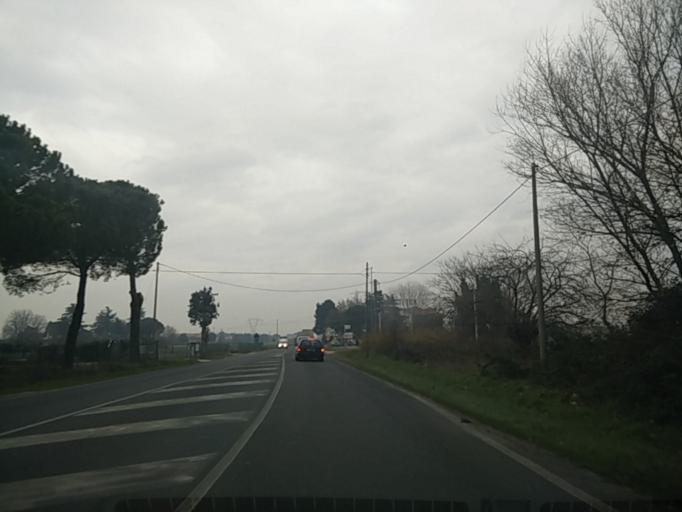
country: IT
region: Emilia-Romagna
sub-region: Provincia di Rimini
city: Santarcangelo
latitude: 44.0734
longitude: 12.4613
